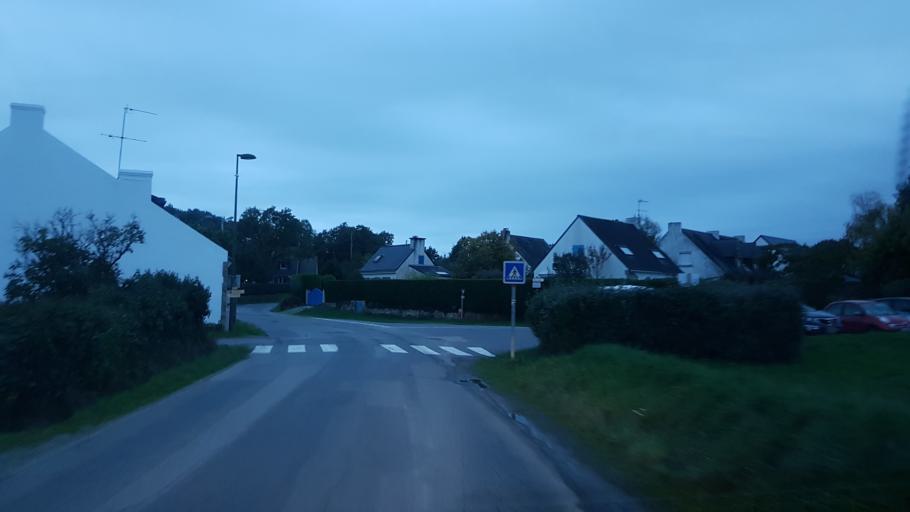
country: FR
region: Brittany
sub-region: Departement du Morbihan
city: Sarzeau
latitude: 47.5409
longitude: -2.8071
